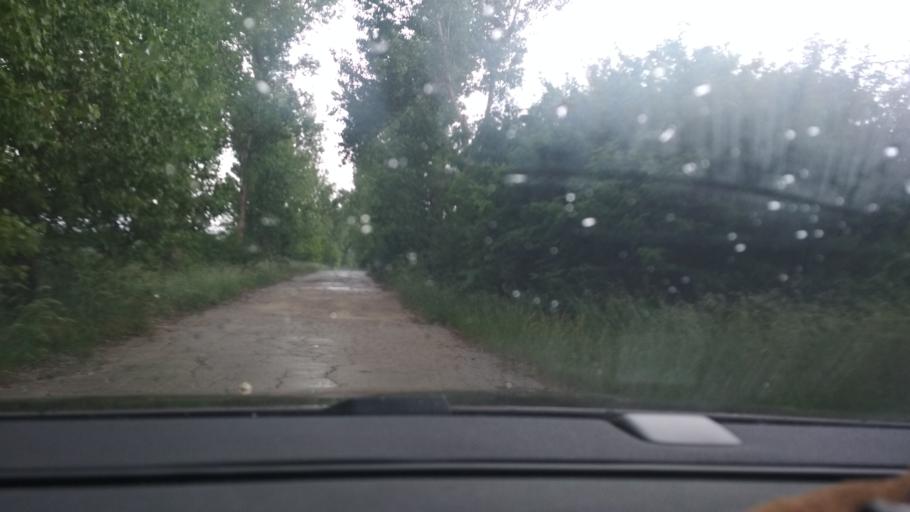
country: MD
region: Singerei
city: Biruinta
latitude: 47.7476
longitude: 28.1396
